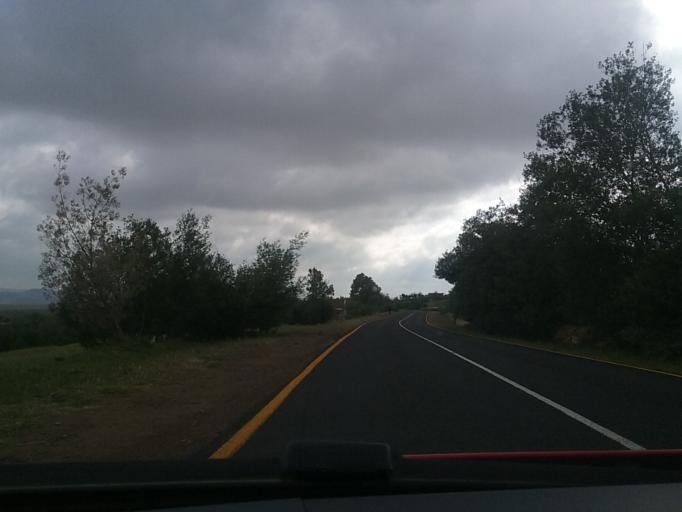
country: LS
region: Berea
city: Teyateyaneng
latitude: -29.1837
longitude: 27.7929
